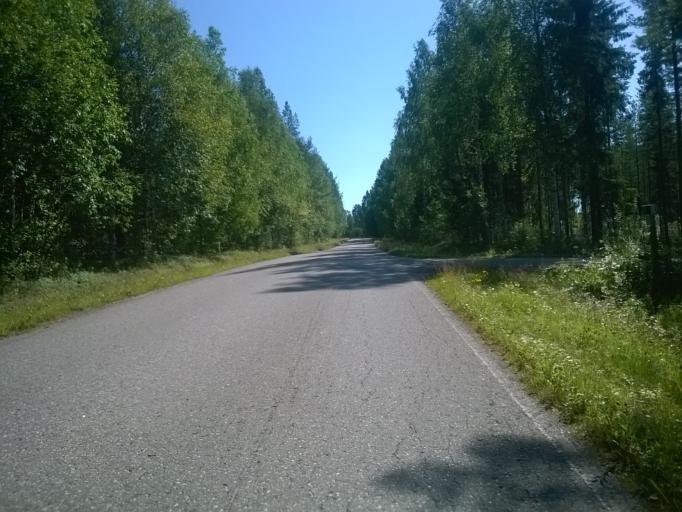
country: FI
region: Kainuu
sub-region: Kehys-Kainuu
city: Kuhmo
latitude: 64.1309
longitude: 29.4453
